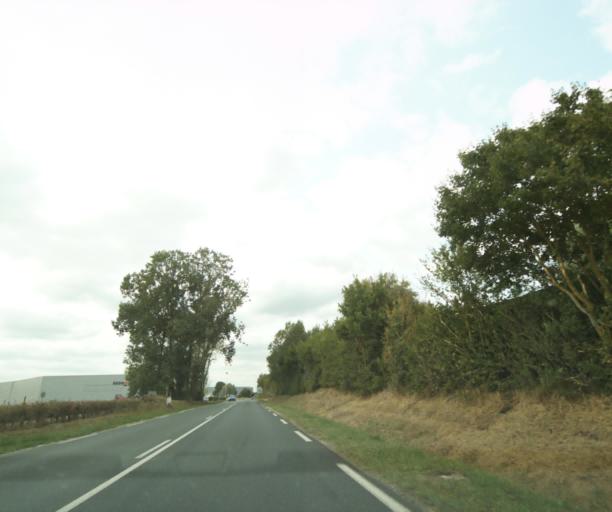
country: FR
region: Centre
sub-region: Departement de l'Indre
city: Buzancais
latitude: 46.8879
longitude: 1.4047
